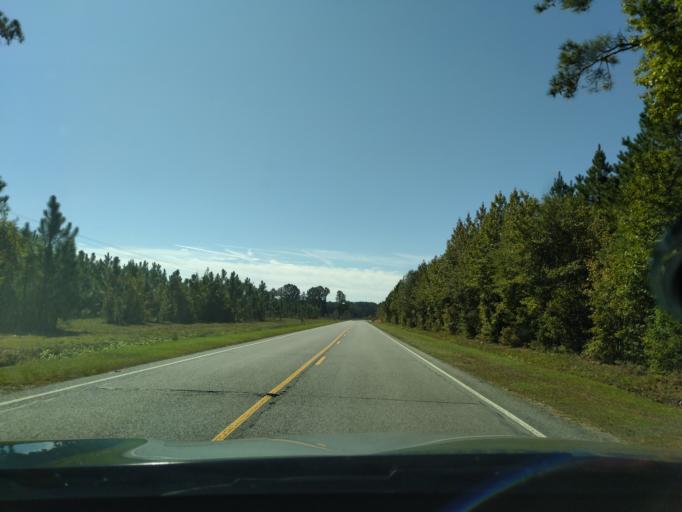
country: US
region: North Carolina
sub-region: Beaufort County
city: Belhaven
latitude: 35.6366
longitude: -76.8047
